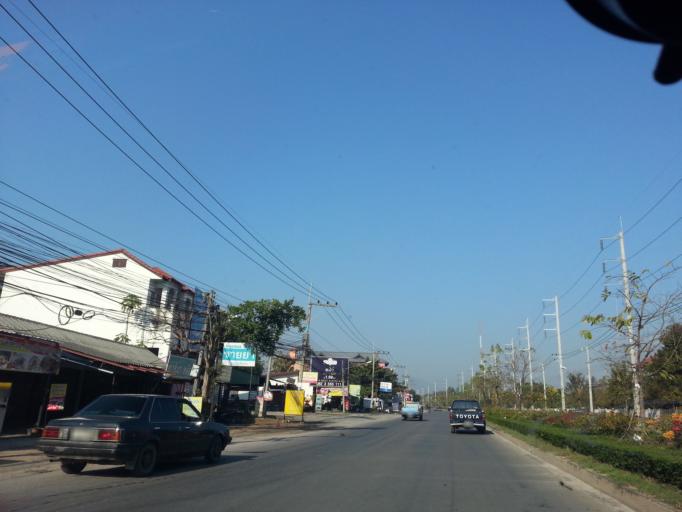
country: TH
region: Chiang Mai
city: San Sai
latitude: 18.8908
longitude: 99.0211
